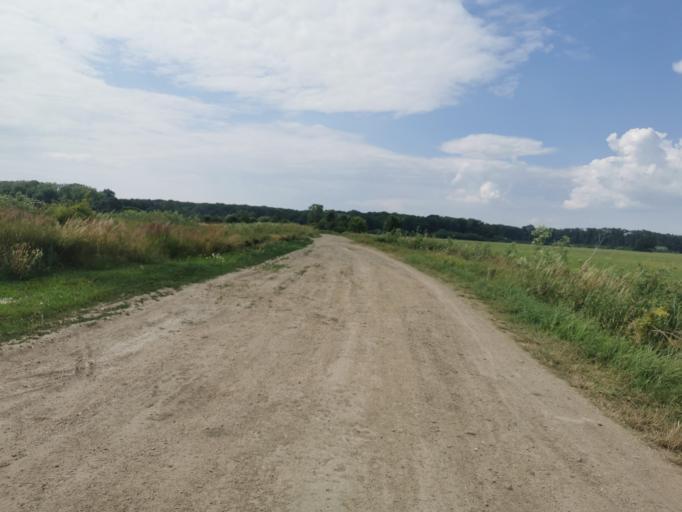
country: CZ
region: South Moravian
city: Rohatec
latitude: 48.8491
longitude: 17.1924
